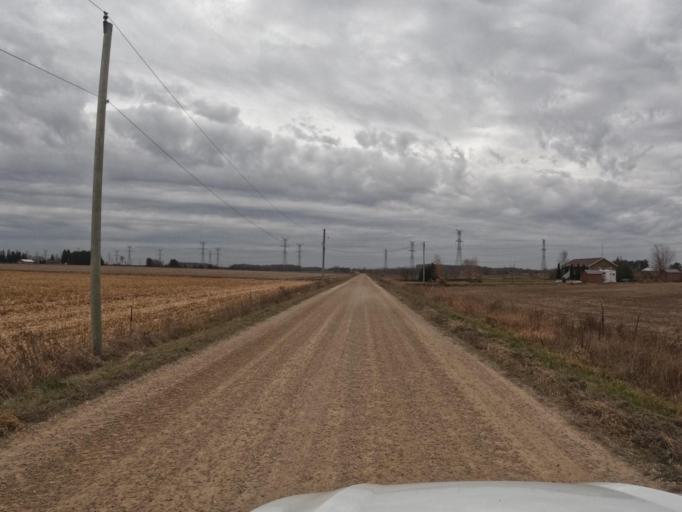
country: CA
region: Ontario
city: Shelburne
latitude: 43.9941
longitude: -80.3856
